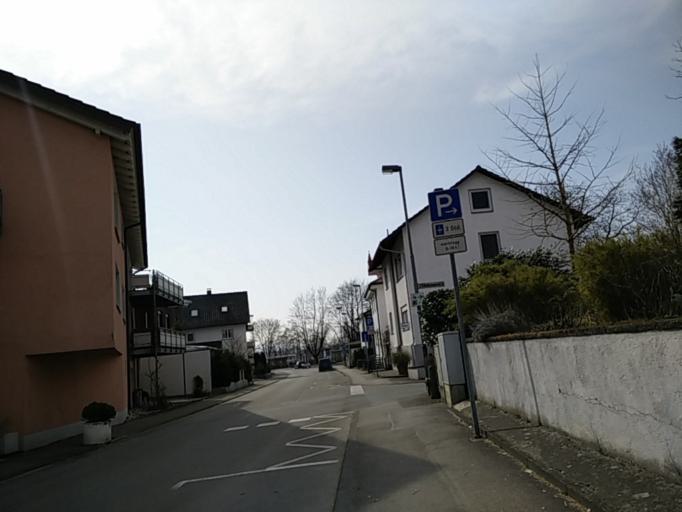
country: DE
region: Baden-Wuerttemberg
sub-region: Freiburg Region
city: Radolfzell am Bodensee
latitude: 47.7405
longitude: 9.0031
